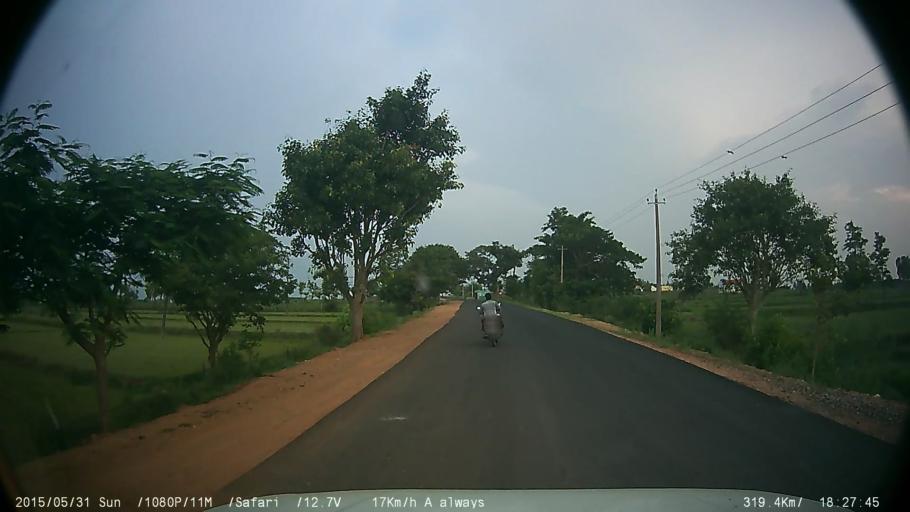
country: IN
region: Karnataka
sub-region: Mysore
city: Nanjangud
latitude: 12.1218
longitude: 76.7179
